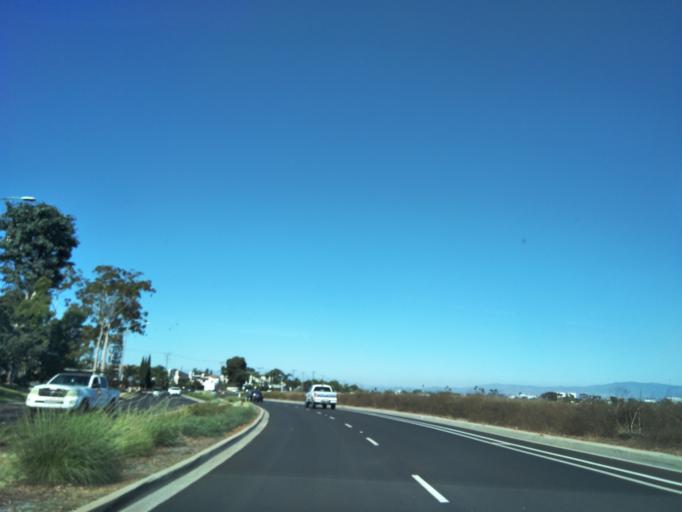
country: US
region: California
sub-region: Orange County
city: Costa Mesa
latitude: 33.6503
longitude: -117.8914
